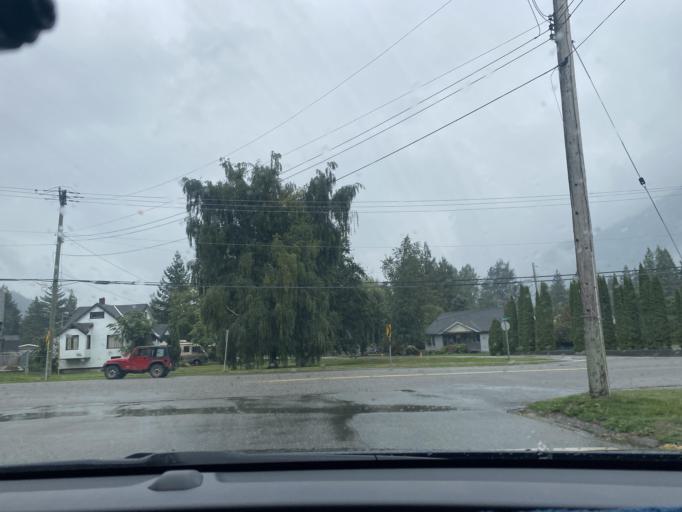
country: CA
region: British Columbia
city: Agassiz
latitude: 49.3027
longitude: -121.7768
